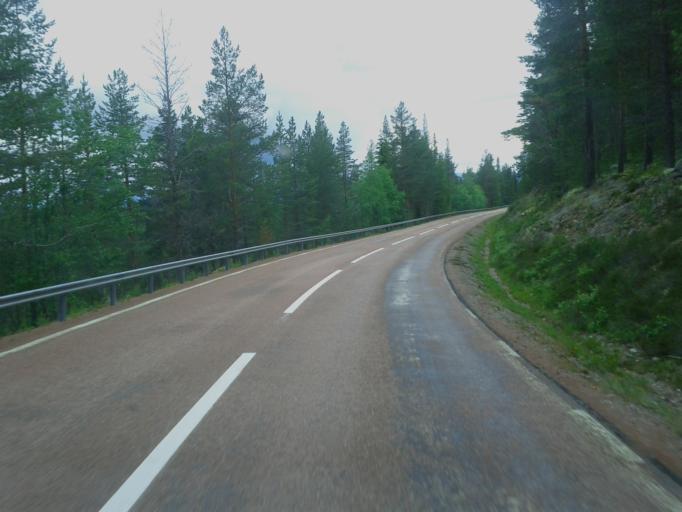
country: NO
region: Hedmark
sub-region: Trysil
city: Innbygda
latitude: 61.8399
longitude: 12.5991
